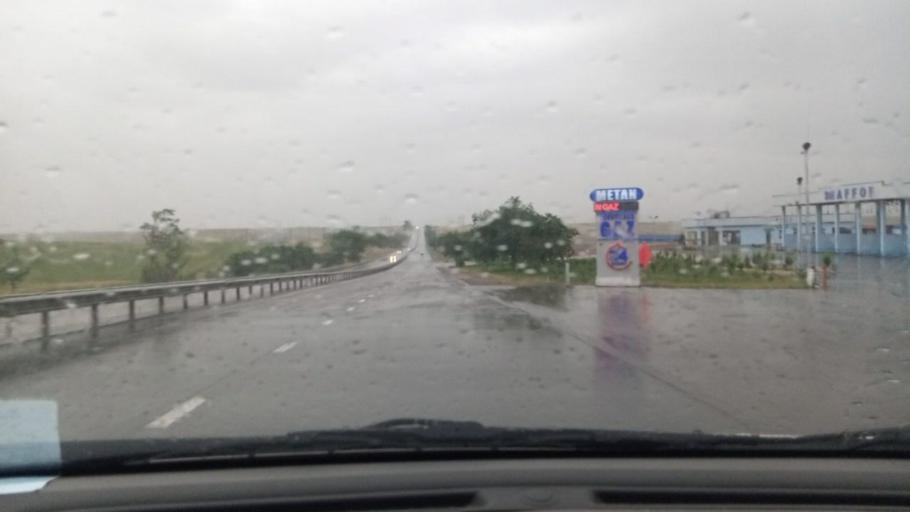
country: UZ
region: Toshkent
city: Ohangaron
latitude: 40.9577
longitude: 69.5618
